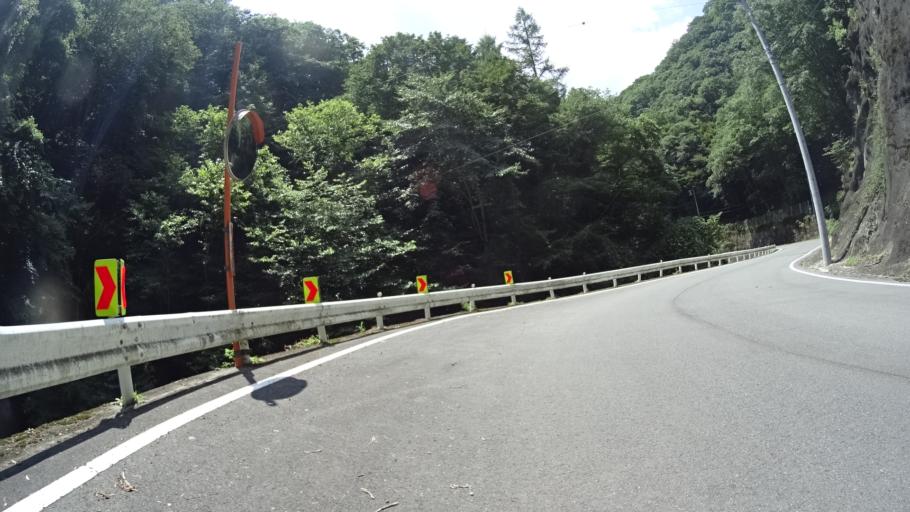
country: JP
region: Nagano
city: Saku
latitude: 36.0699
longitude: 138.7013
